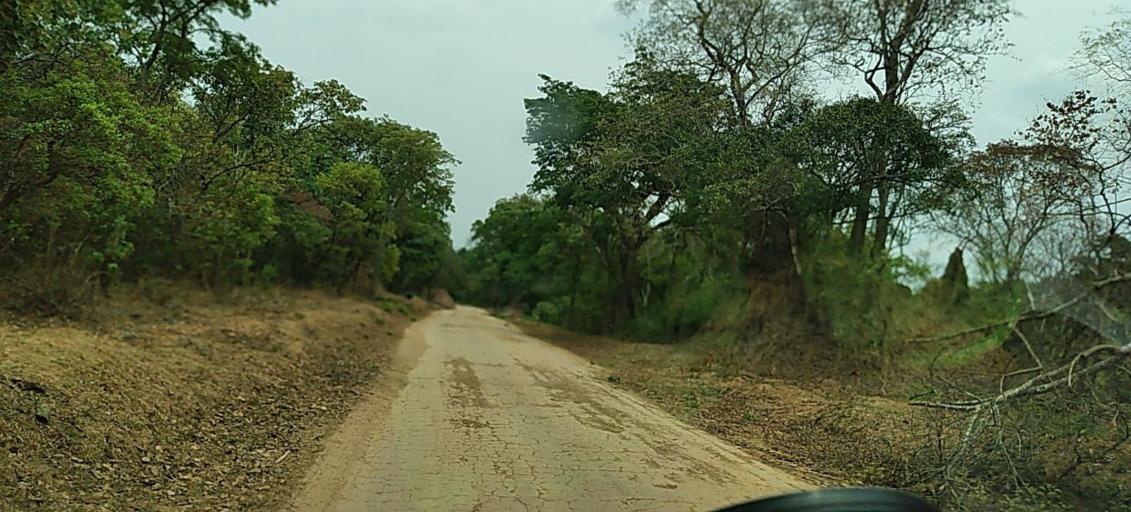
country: ZM
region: North-Western
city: Solwezi
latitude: -12.7849
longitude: 26.5230
